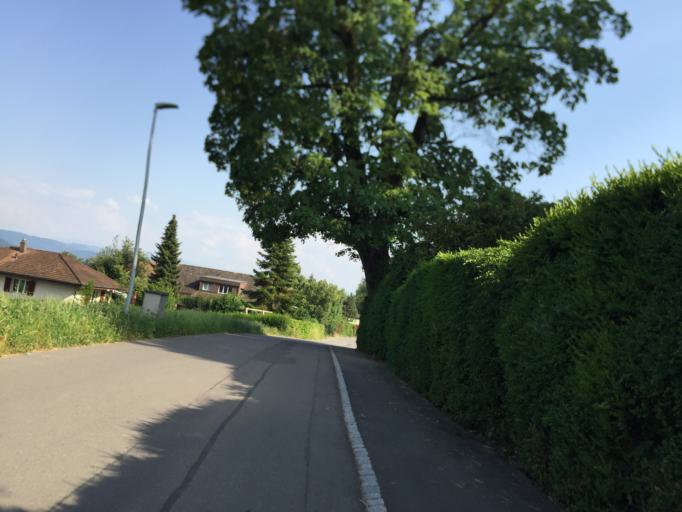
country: CH
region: Bern
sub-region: Bern-Mittelland District
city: Rubigen
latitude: 46.9167
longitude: 7.5231
